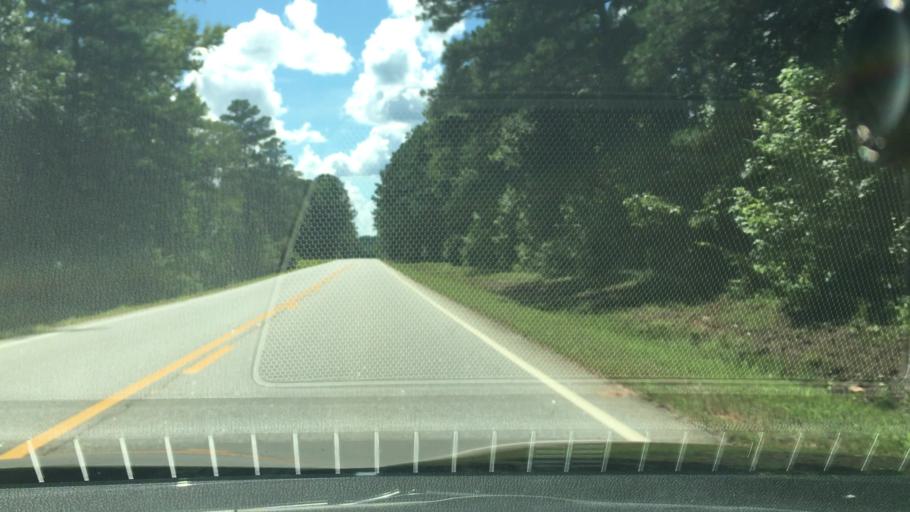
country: US
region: Georgia
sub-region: Butts County
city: Indian Springs
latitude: 33.3072
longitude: -83.8247
